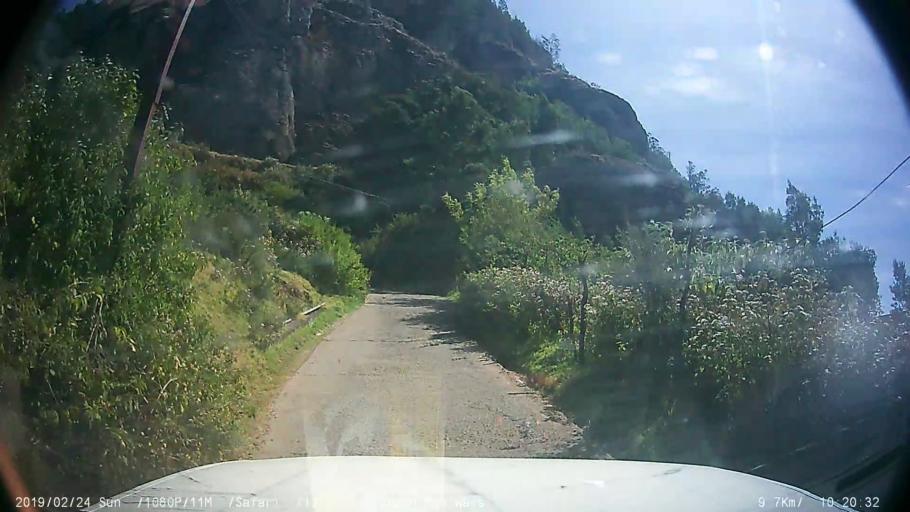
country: IN
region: Tamil Nadu
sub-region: Nilgiri
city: Ooty
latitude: 11.3895
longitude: 76.7197
